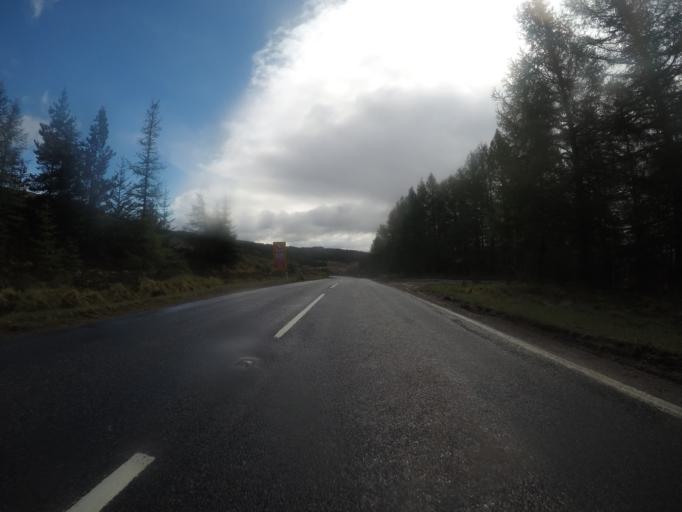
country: GB
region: Scotland
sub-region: Highland
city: Spean Bridge
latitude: 57.0875
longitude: -4.9731
